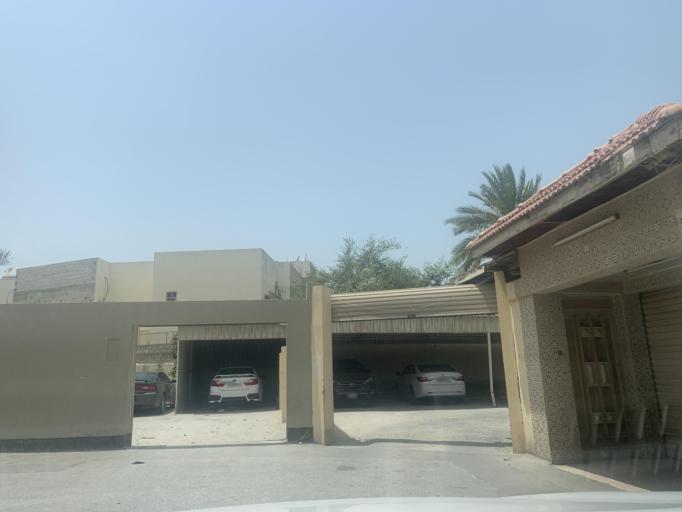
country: BH
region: Manama
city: Jidd Hafs
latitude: 26.2188
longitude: 50.4630
